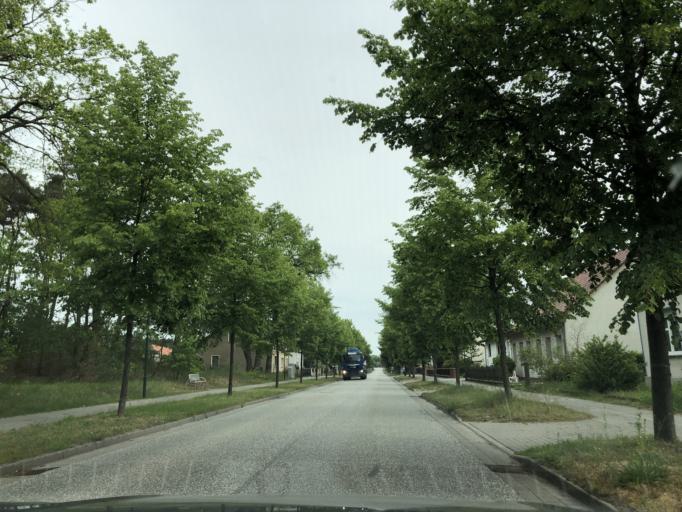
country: DE
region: Brandenburg
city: Plattenburg
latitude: 52.9131
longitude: 12.0854
